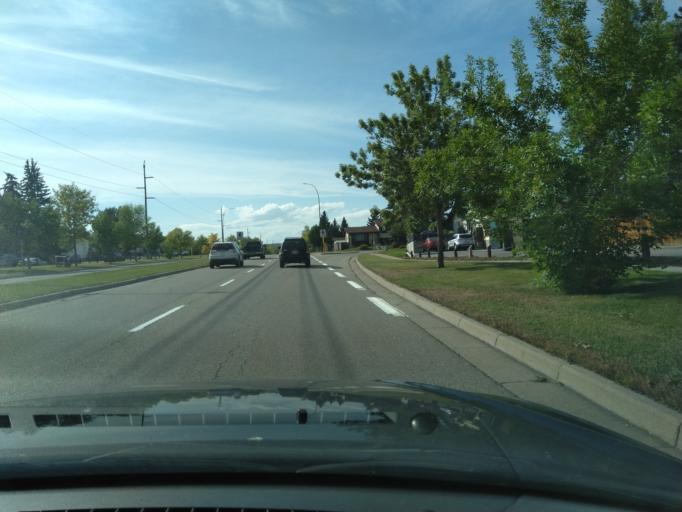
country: CA
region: Alberta
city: Calgary
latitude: 51.1252
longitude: -114.0615
